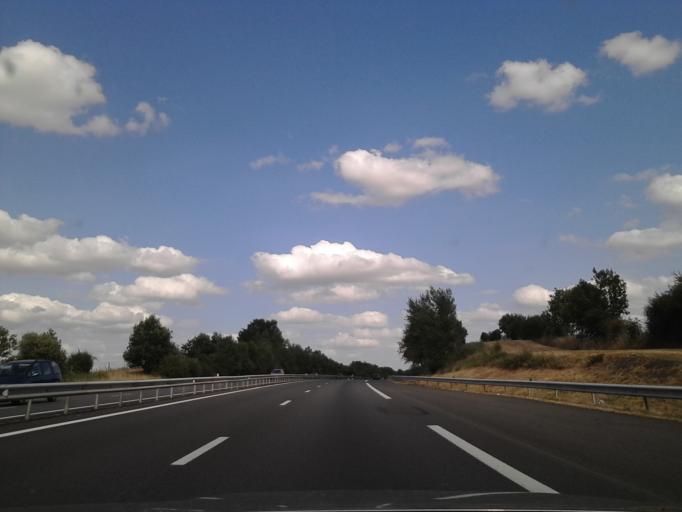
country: FR
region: Auvergne
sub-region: Departement de l'Allier
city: Montmarault
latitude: 46.3311
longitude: 2.9018
